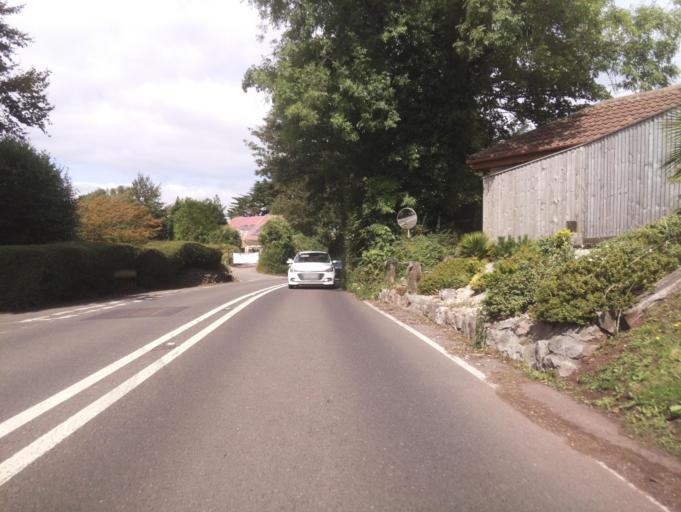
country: GB
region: England
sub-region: Borough of Torbay
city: Torquay
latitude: 50.5062
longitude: -3.5254
